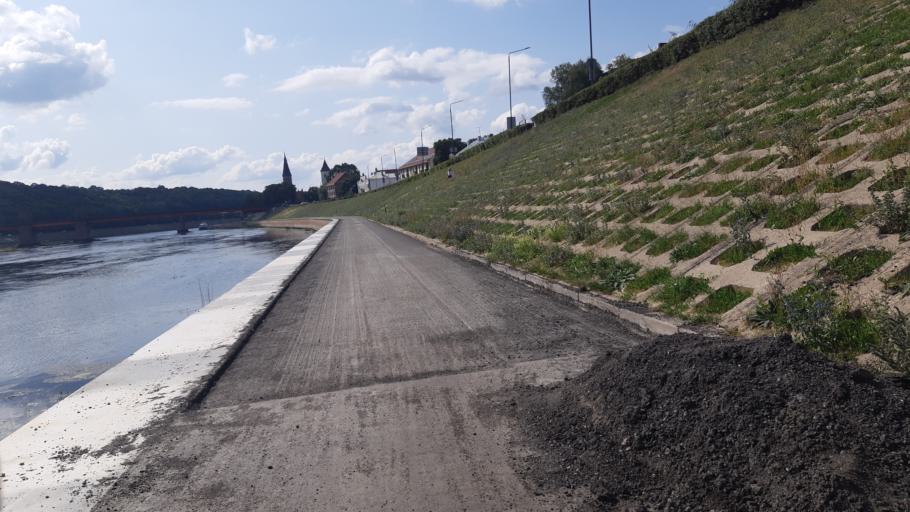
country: LT
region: Kauno apskritis
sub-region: Kaunas
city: Kaunas
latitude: 54.8944
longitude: 23.8950
